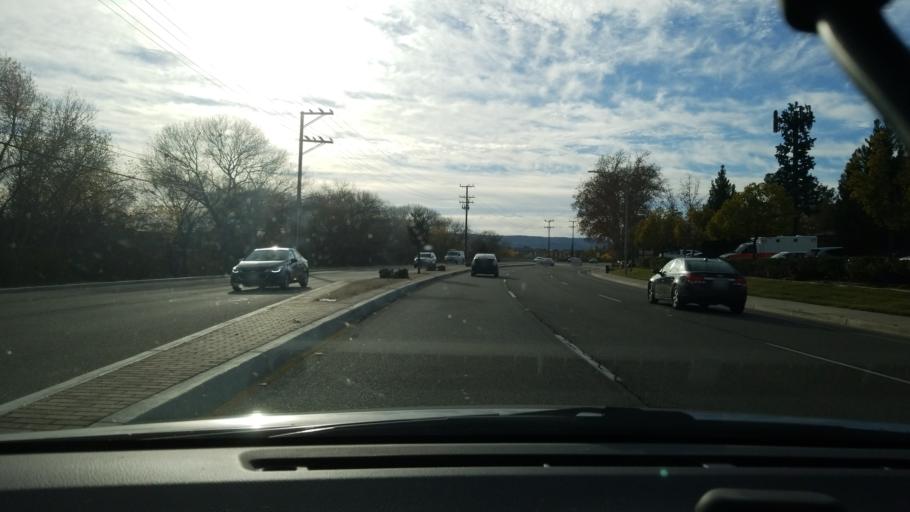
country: US
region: California
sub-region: Riverside County
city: Murrieta Hot Springs
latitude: 33.5549
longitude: -117.1643
